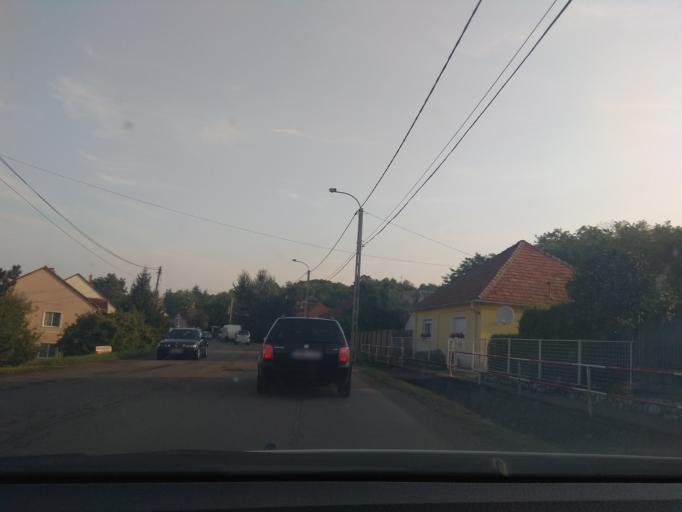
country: HU
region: Heves
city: Andornaktalya
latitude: 47.8637
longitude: 20.4073
